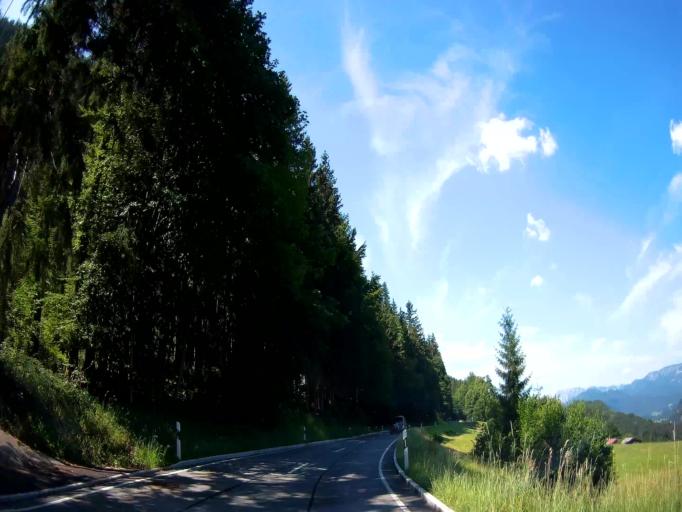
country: AT
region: Salzburg
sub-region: Politischer Bezirk Hallein
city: Hallein
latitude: 47.6407
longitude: 13.0610
